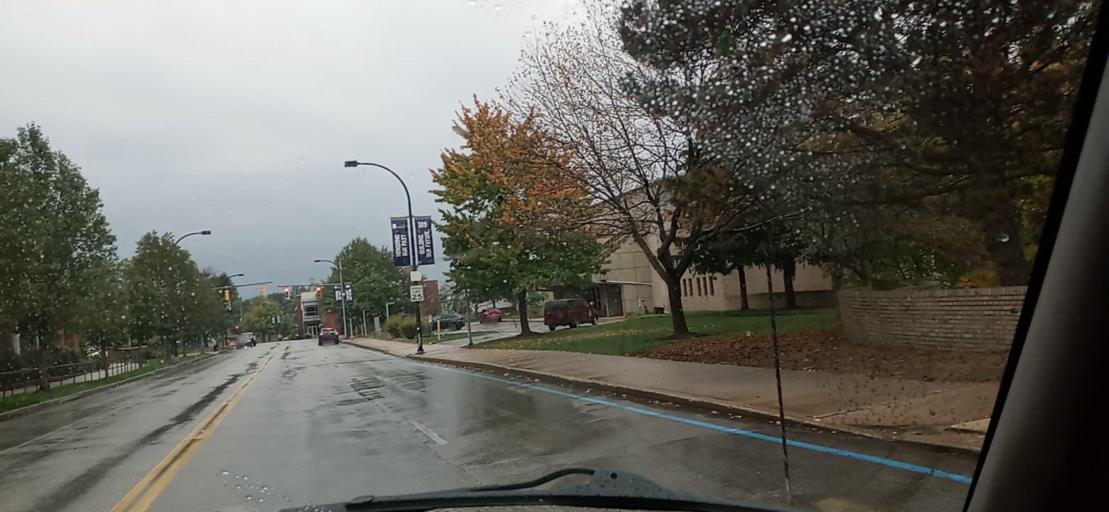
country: US
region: Ohio
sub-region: Summit County
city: Akron
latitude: 41.0778
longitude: -81.5159
